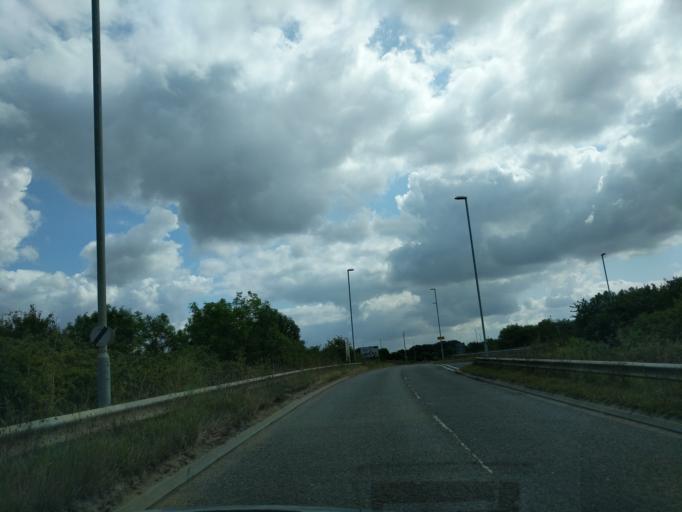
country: GB
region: England
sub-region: Cambridgeshire
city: Isleham
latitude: 52.2896
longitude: 0.4685
